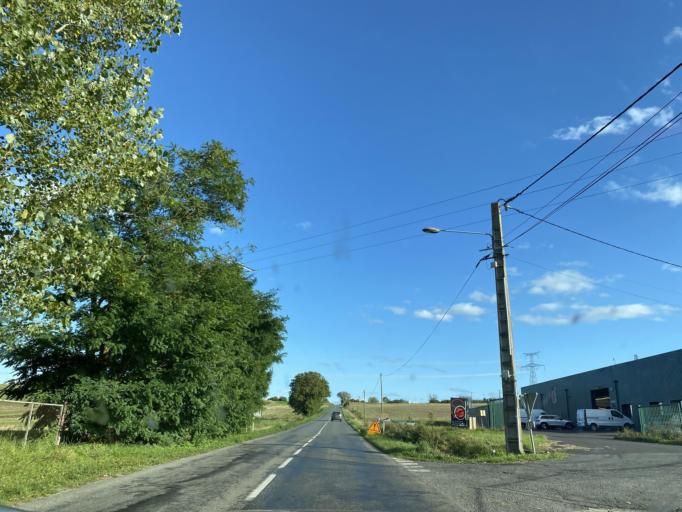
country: FR
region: Auvergne
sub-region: Departement de l'Allier
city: Gannat
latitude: 46.0710
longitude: 3.2791
